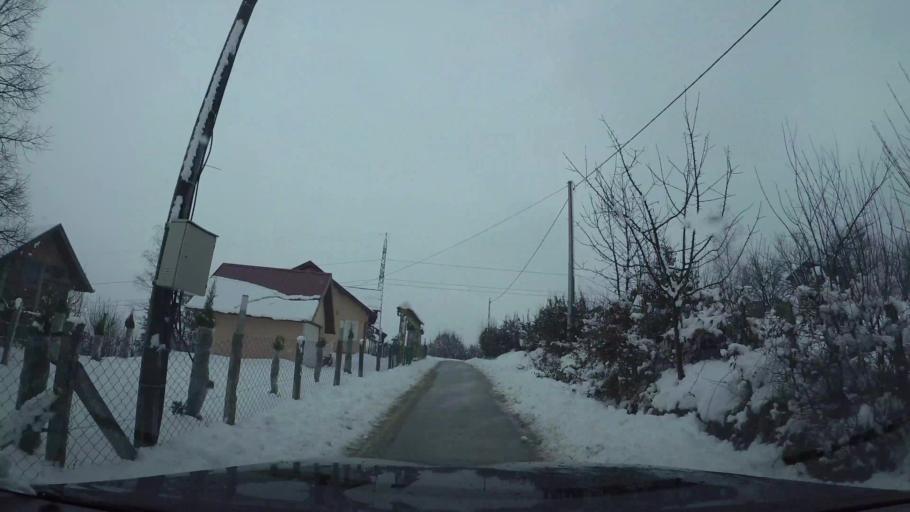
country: BA
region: Federation of Bosnia and Herzegovina
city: Hadzici
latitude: 43.8548
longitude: 18.2627
